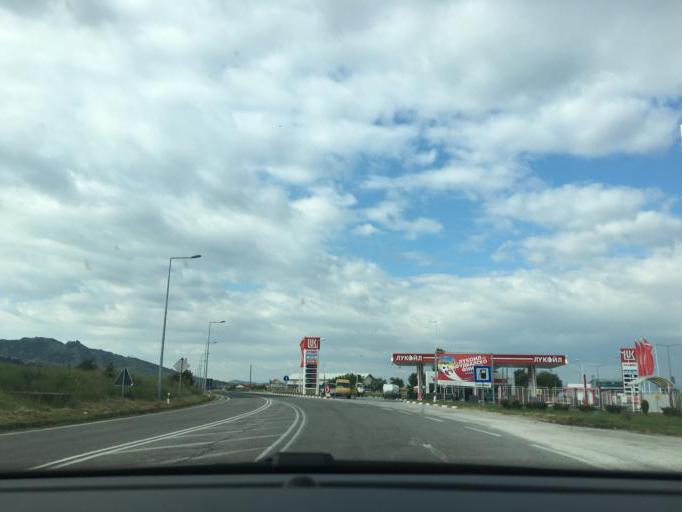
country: MK
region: Prilep
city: Prilep
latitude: 41.3565
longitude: 21.5804
